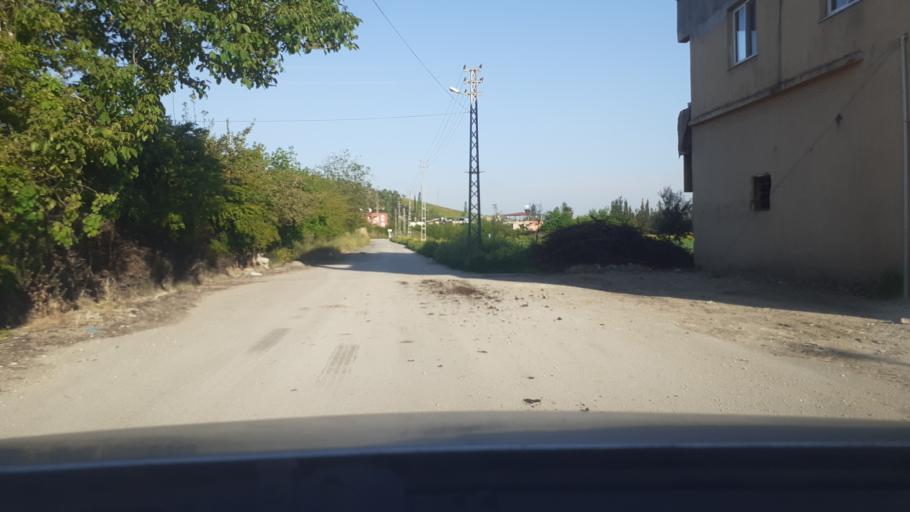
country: TR
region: Hatay
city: Kirikhan
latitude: 36.4749
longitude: 36.3171
